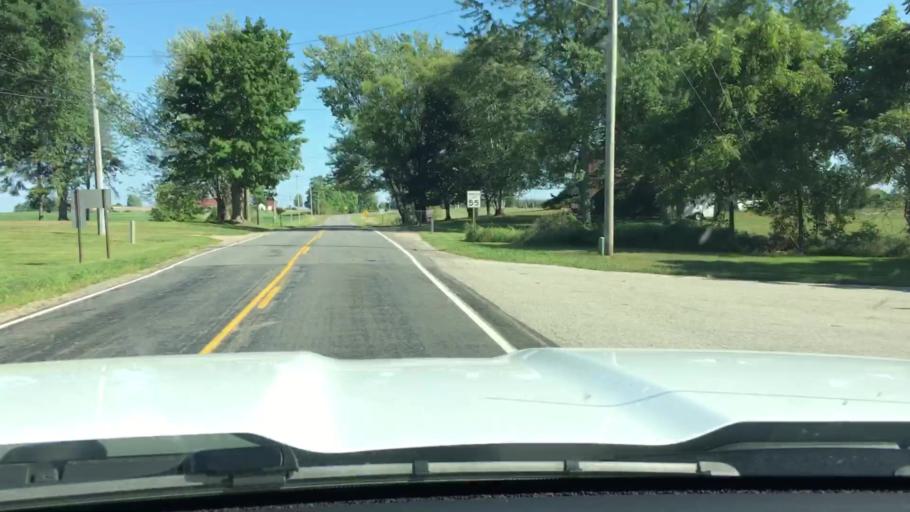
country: US
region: Michigan
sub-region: Muskegon County
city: Ravenna
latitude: 43.1844
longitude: -85.9321
